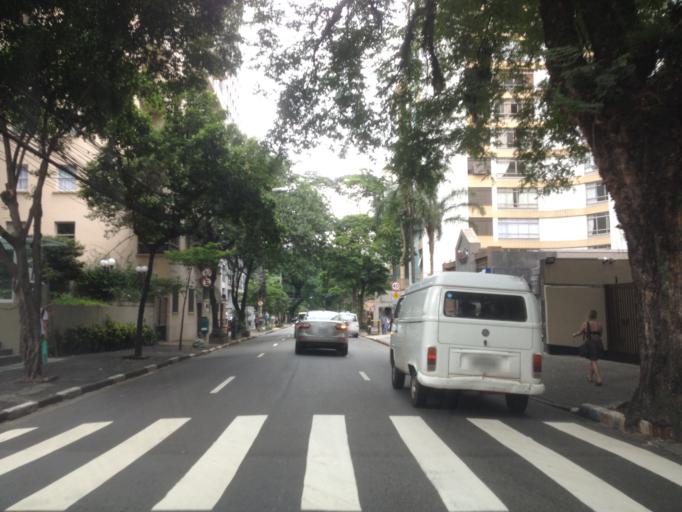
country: BR
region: Sao Paulo
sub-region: Sao Paulo
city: Sao Paulo
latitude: -23.5574
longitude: -46.6630
